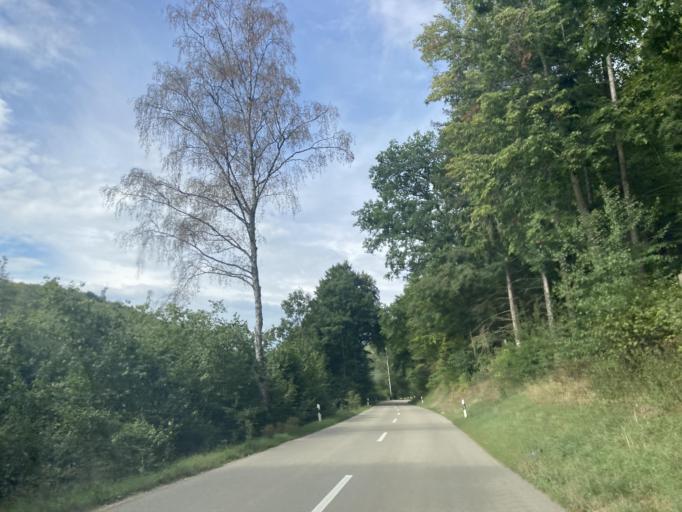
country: DE
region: Bavaria
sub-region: Swabia
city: Forheim
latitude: 48.7855
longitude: 10.4740
